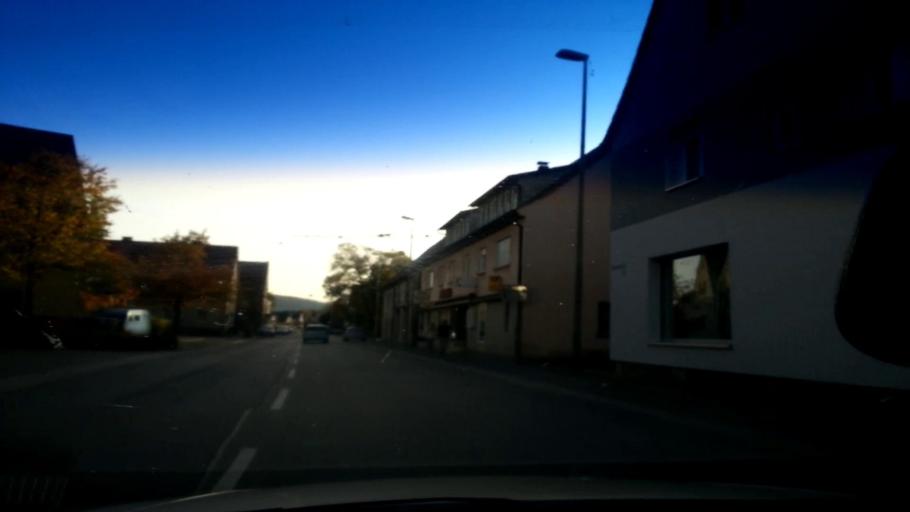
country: DE
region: Bavaria
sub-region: Upper Franconia
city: Zapfendorf
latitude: 50.0201
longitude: 10.9325
